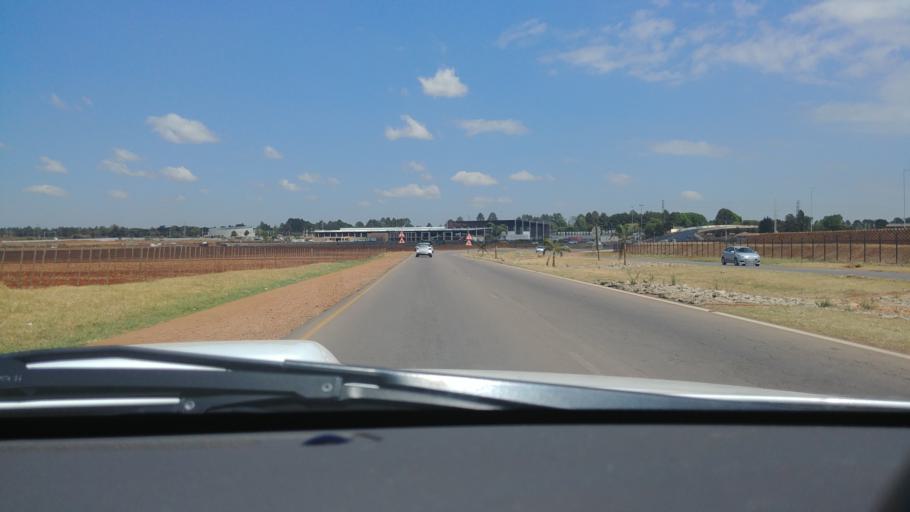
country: ZA
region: Gauteng
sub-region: Ekurhuleni Metropolitan Municipality
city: Tembisa
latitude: -26.0326
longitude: 28.2629
